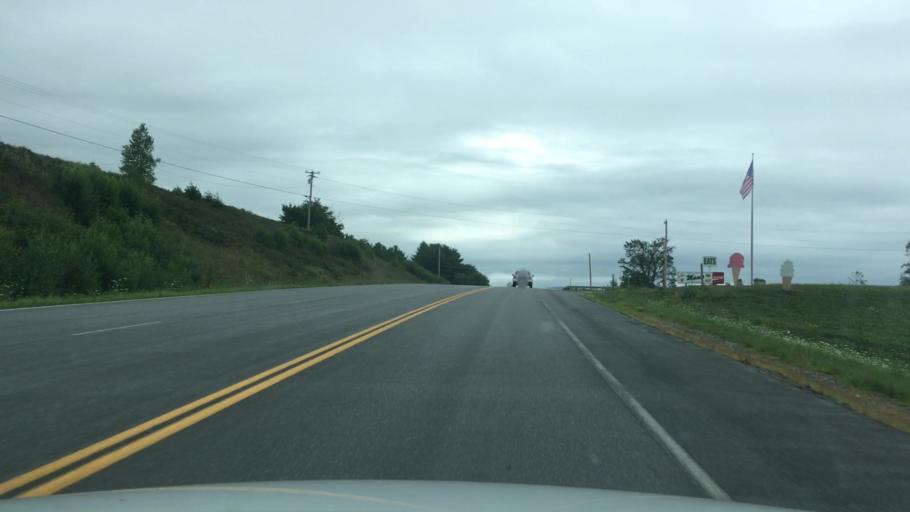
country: US
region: Maine
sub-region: Hancock County
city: Franklin
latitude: 44.8583
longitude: -68.3180
